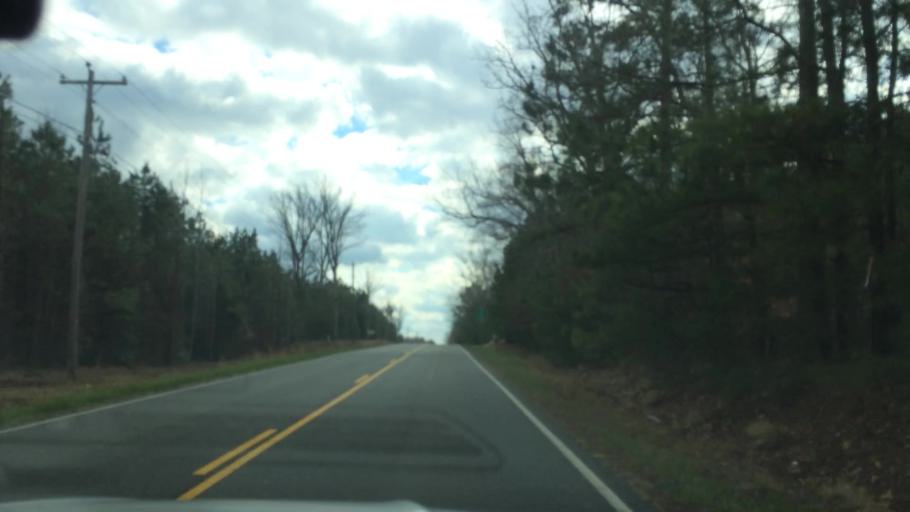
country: US
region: Virginia
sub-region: New Kent County
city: New Kent
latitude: 37.5050
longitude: -77.0185
